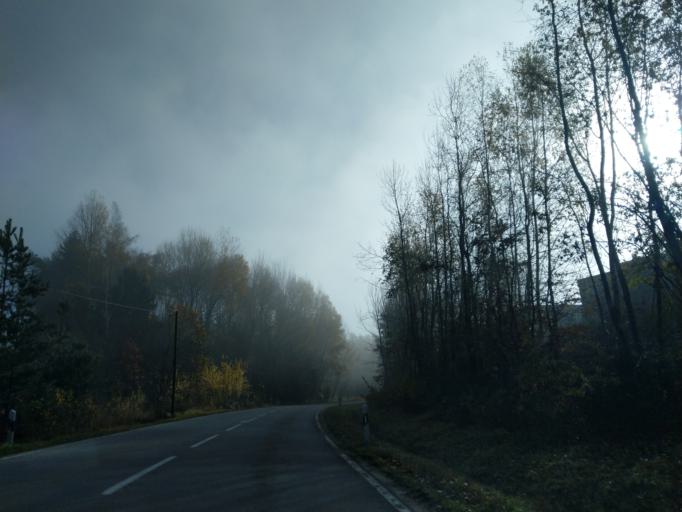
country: DE
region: Bavaria
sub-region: Lower Bavaria
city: Aussernzell
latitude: 48.7232
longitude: 13.2288
